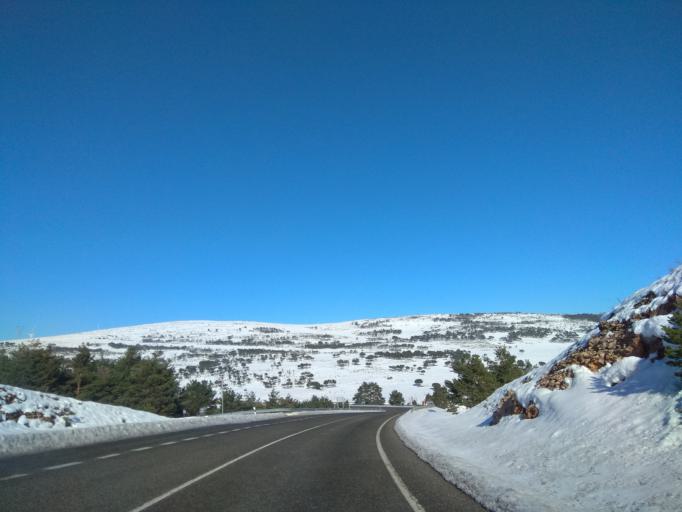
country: ES
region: Castille and Leon
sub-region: Provincia de Burgos
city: Medina de Pomar
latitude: 42.9338
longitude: -3.6594
